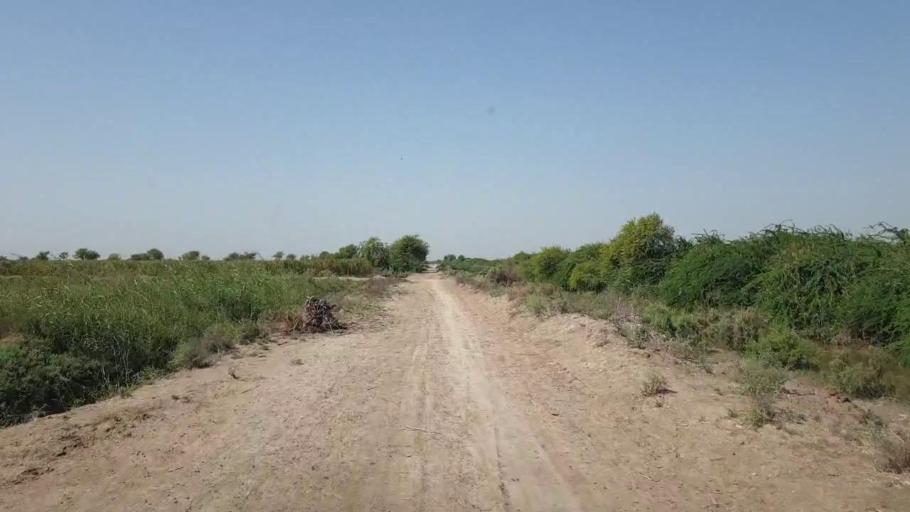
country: PK
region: Sindh
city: Tando Bago
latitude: 24.7449
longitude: 69.0293
